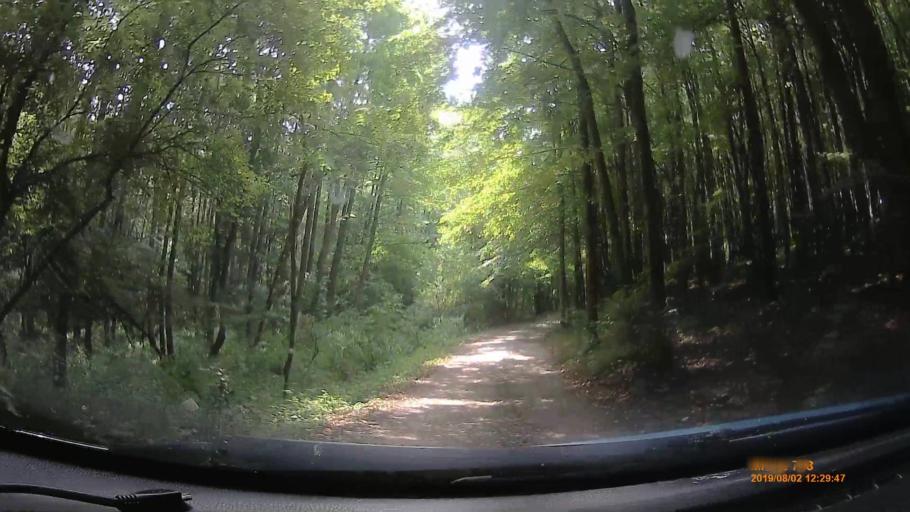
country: HU
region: Baranya
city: Buekkoesd
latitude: 46.1111
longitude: 17.9355
